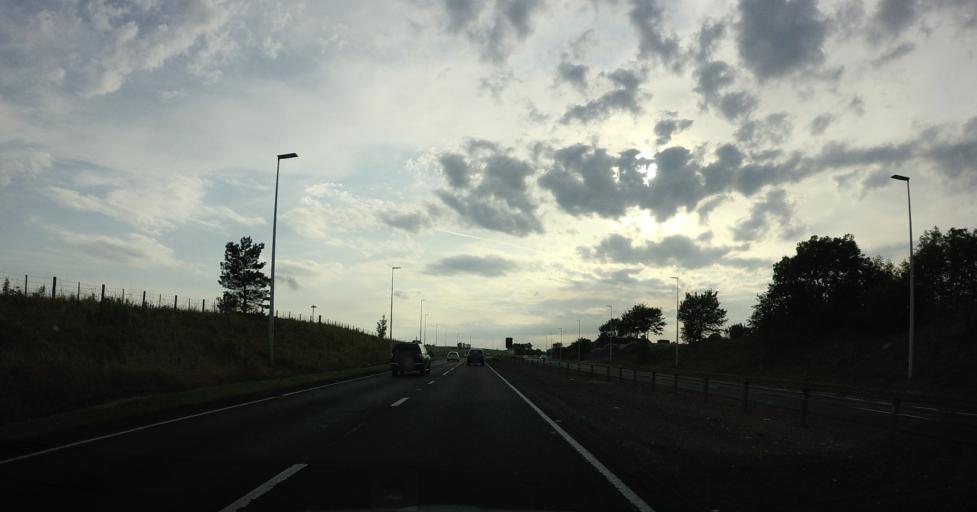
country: GB
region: Scotland
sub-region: Perth and Kinross
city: Auchterarder
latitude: 56.2573
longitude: -3.7832
